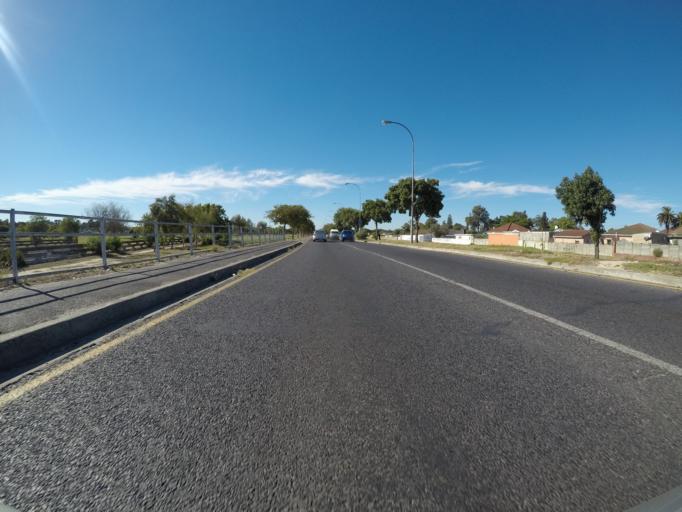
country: ZA
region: Western Cape
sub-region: City of Cape Town
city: Kraaifontein
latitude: -33.9301
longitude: 18.6767
